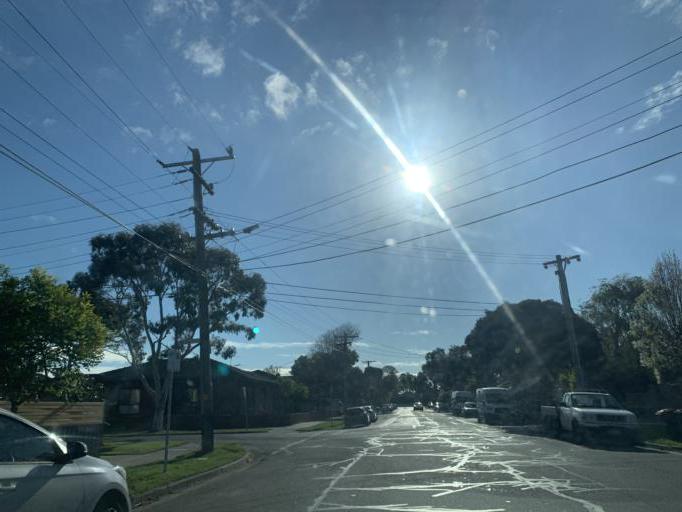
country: AU
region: Victoria
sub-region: Kingston
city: Mentone
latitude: -37.9824
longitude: 145.0609
